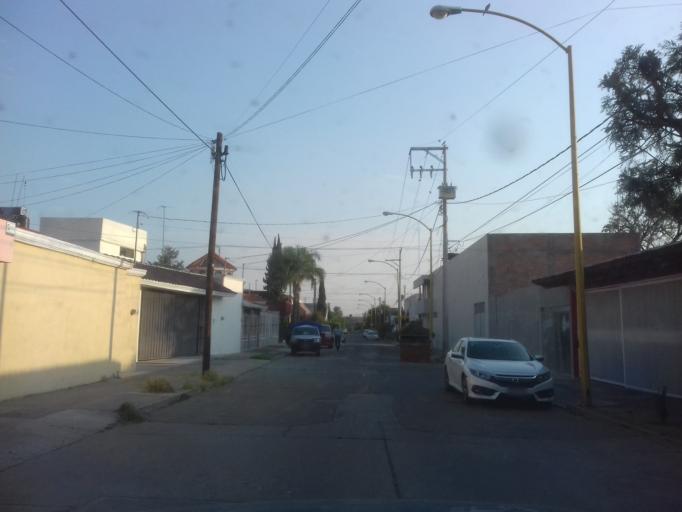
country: MX
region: Aguascalientes
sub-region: Aguascalientes
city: Aguascalientes
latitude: 21.8603
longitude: -102.2925
